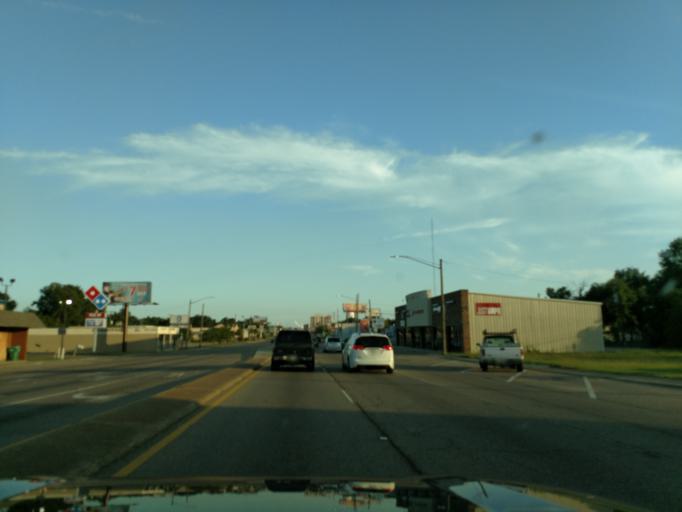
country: US
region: Mississippi
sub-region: Harrison County
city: Gulfport
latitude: 30.3838
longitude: -89.0932
